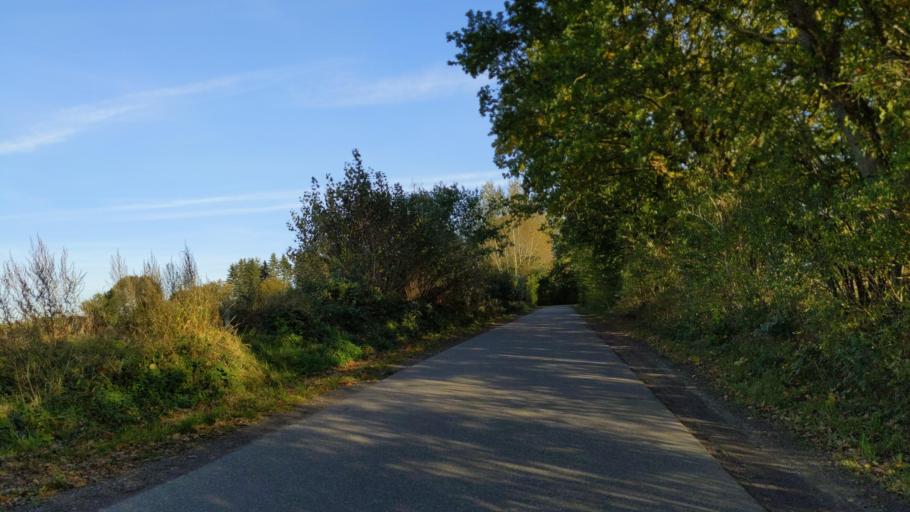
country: DE
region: Schleswig-Holstein
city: Susel
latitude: 54.0879
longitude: 10.6522
